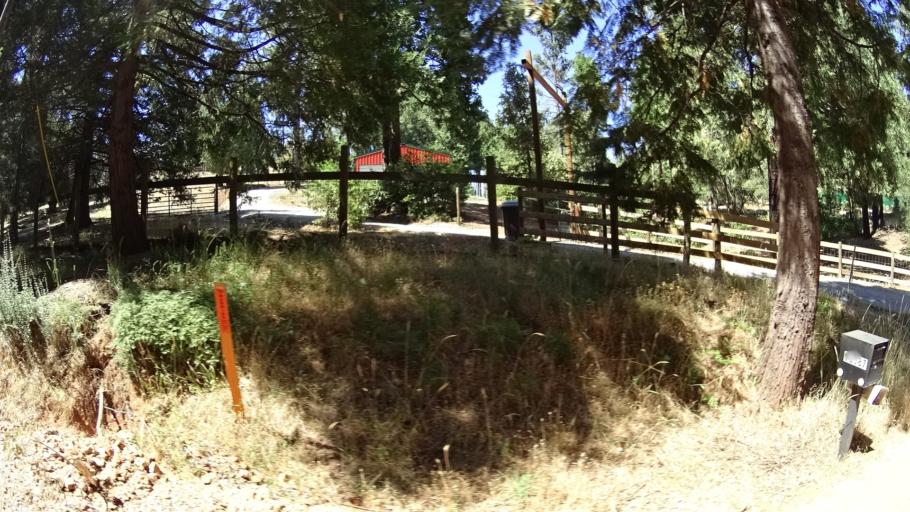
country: US
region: California
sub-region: Calaveras County
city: Mountain Ranch
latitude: 38.2836
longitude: -120.5524
